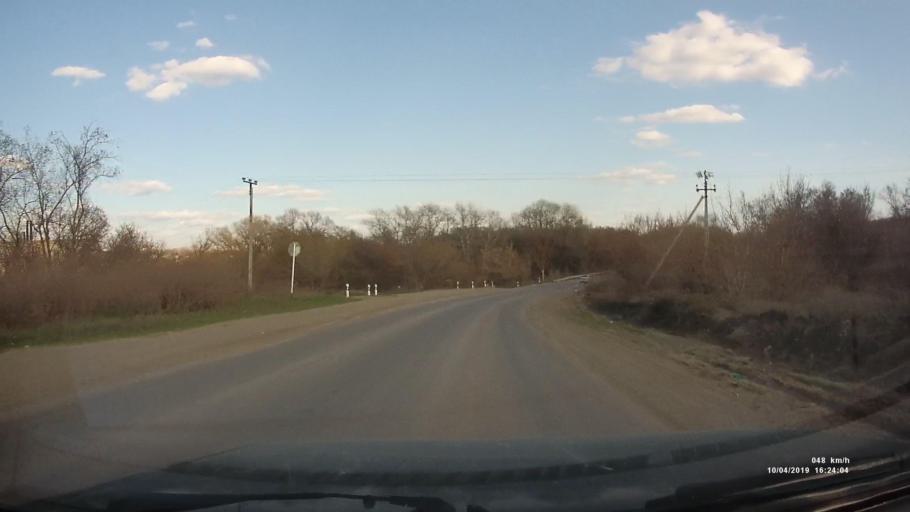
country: RU
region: Rostov
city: Staraya Stanitsa
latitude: 48.3018
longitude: 40.3118
